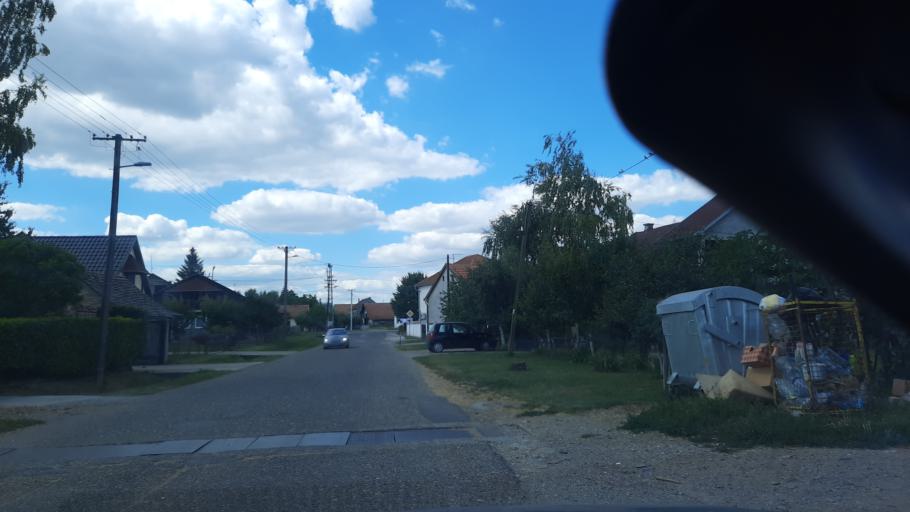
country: RS
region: Autonomna Pokrajina Vojvodina
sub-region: Sremski Okrug
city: Pecinci
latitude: 44.9142
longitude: 19.9681
